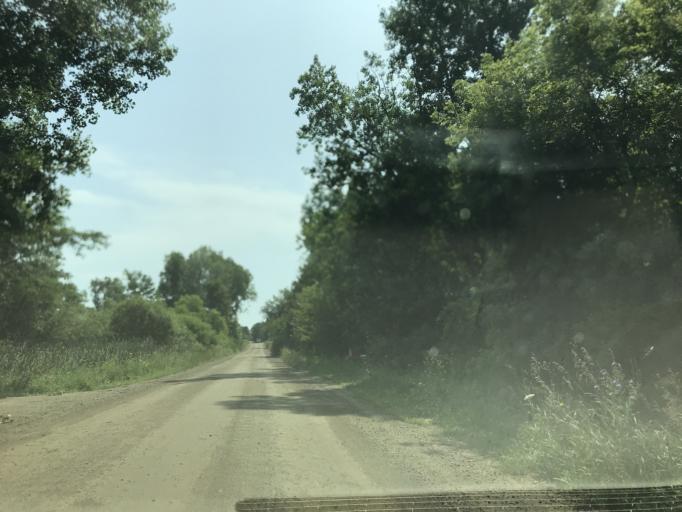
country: US
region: Michigan
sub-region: Eaton County
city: Grand Ledge
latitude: 42.7701
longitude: -84.7110
